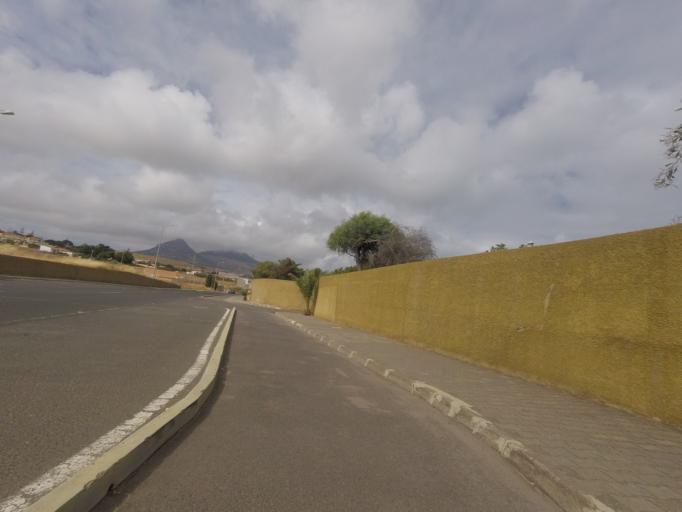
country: PT
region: Madeira
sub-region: Porto Santo
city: Vila de Porto Santo
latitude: 33.0470
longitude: -16.3548
